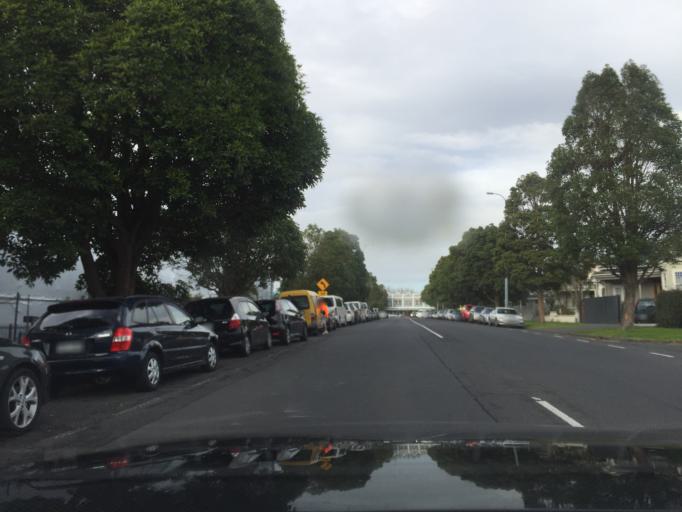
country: NZ
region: Auckland
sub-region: Auckland
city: Auckland
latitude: -36.8565
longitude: 174.7302
